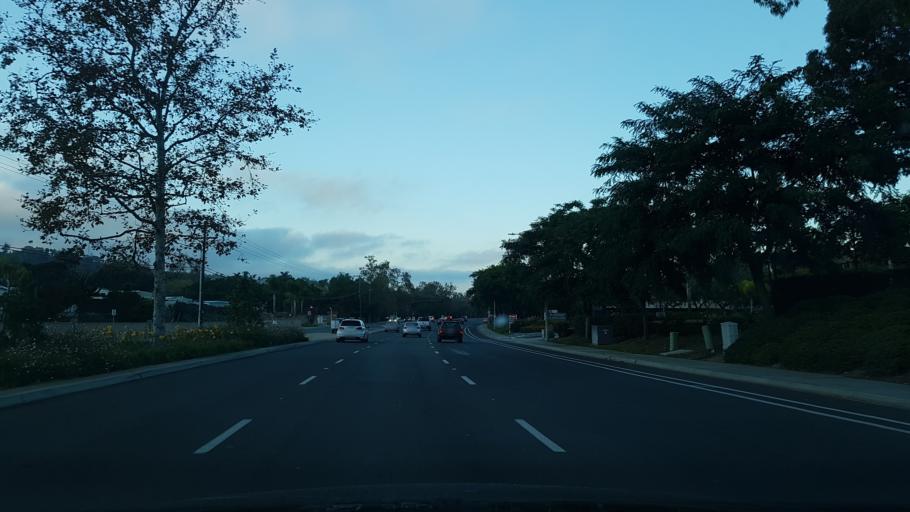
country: US
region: California
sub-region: San Diego County
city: Encinitas
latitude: 33.0559
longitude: -117.2622
